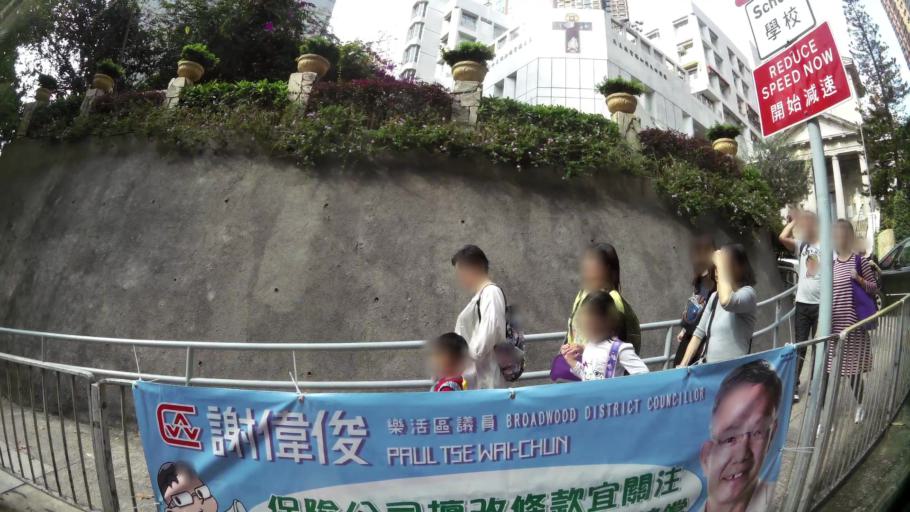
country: HK
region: Wanchai
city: Wan Chai
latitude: 22.2741
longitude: 114.1839
